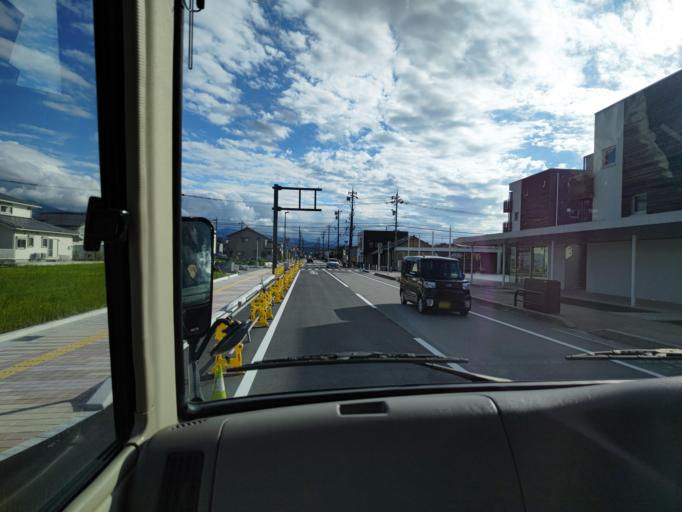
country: JP
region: Toyama
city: Nyuzen
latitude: 36.8775
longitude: 137.4467
